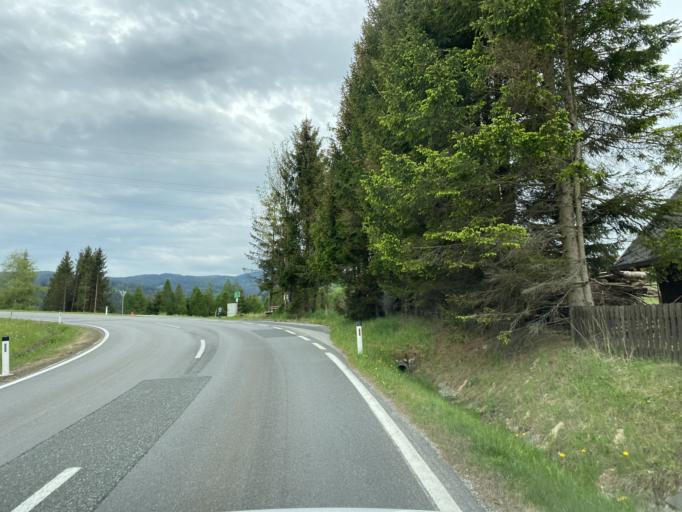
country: AT
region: Styria
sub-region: Politischer Bezirk Weiz
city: Birkfeld
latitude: 47.3466
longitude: 15.7037
